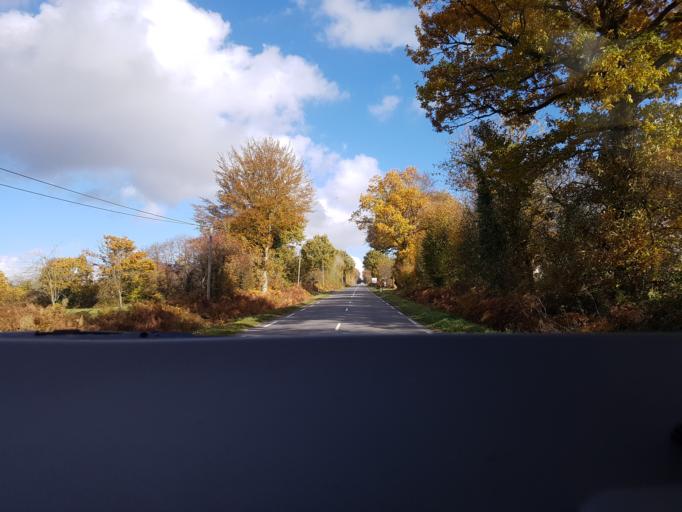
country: FR
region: Lower Normandy
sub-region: Departement de l'Orne
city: La Ferriere-aux-Etangs
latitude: 48.6526
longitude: -0.5310
